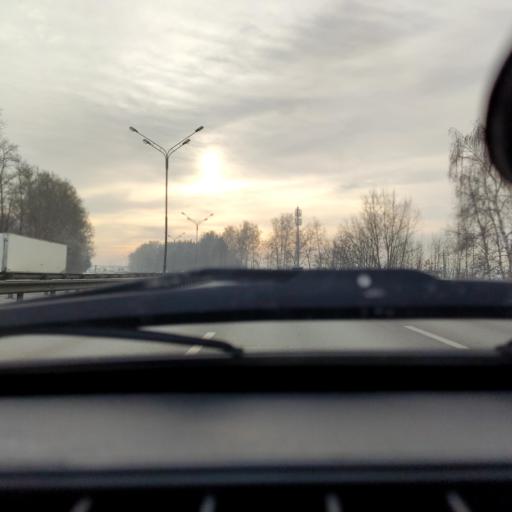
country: RU
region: Bashkortostan
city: Ufa
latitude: 54.6263
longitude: 55.9249
